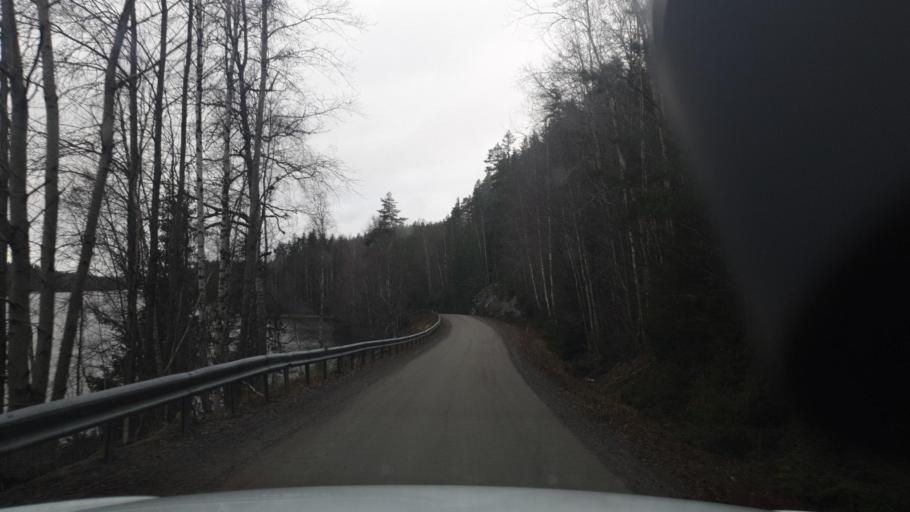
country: SE
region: Vaermland
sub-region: Sunne Kommun
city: Sunne
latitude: 59.6319
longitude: 13.0632
